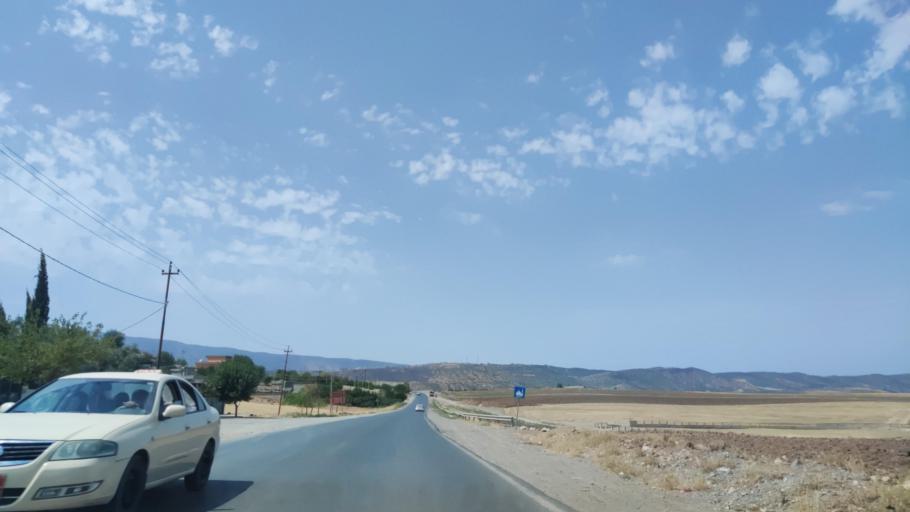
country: IQ
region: Arbil
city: Shaqlawah
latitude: 36.4659
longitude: 44.3958
